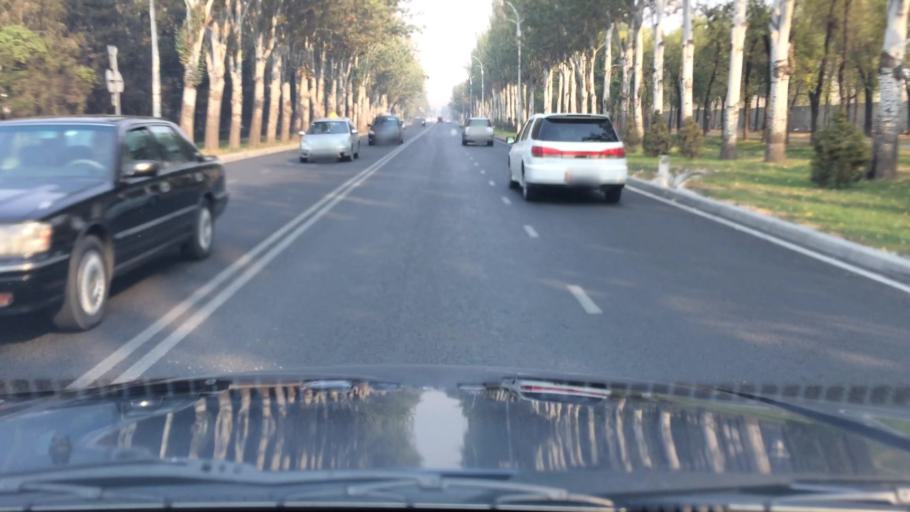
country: KG
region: Chuy
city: Bishkek
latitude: 42.8374
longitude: 74.5858
